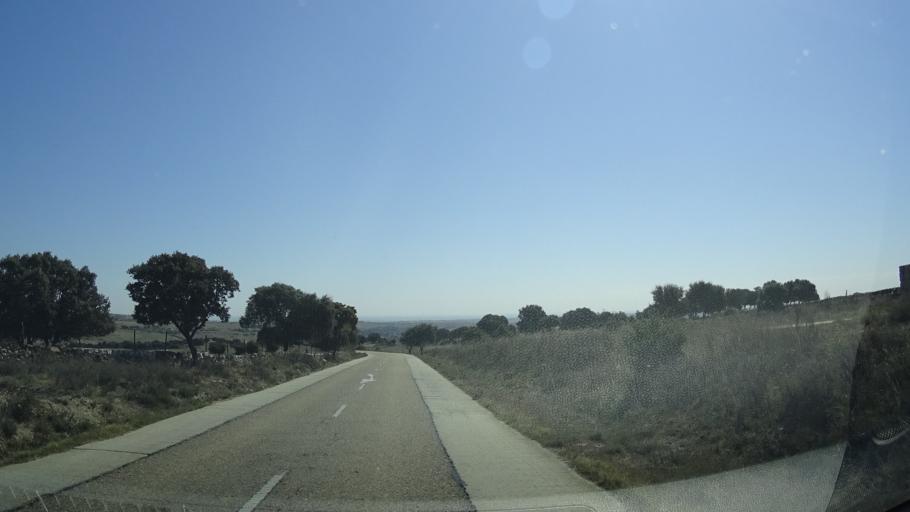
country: ES
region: Madrid
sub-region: Provincia de Madrid
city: Colmenar Viejo
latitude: 40.6450
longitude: -3.8208
